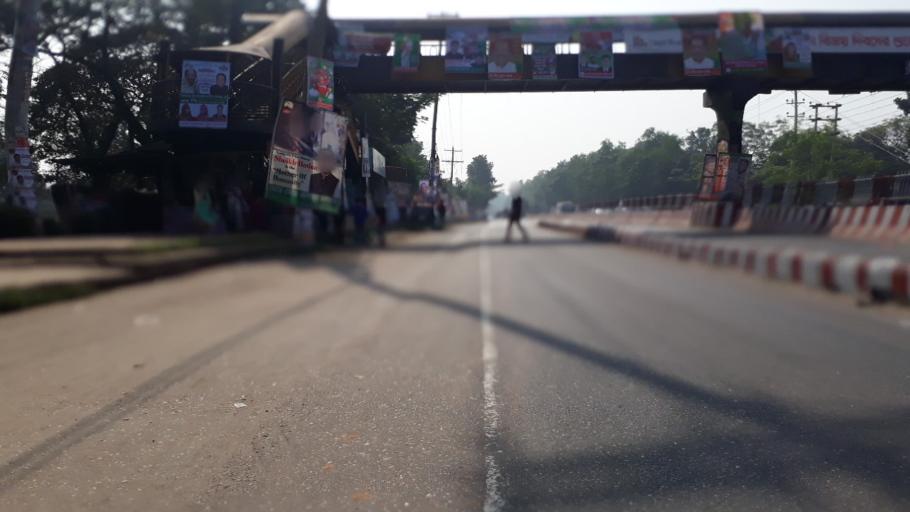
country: BD
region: Dhaka
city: Tungi
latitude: 23.8800
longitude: 90.2732
